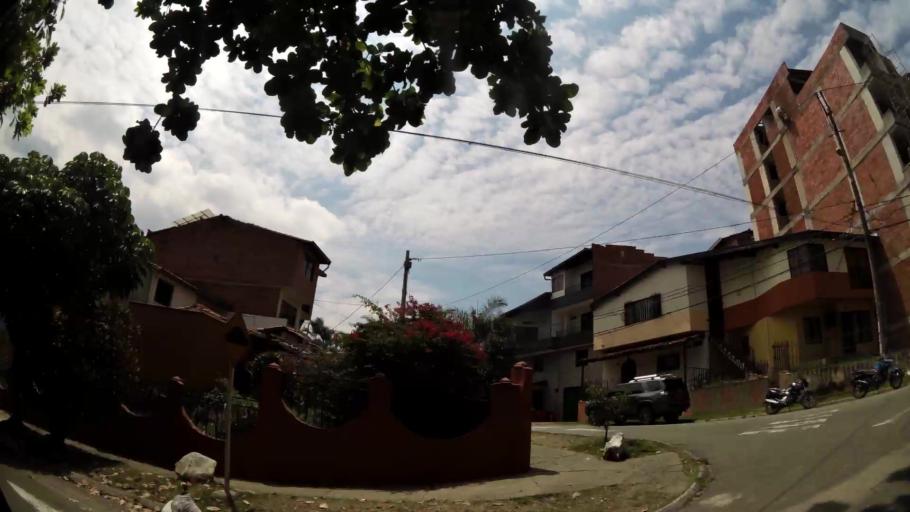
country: CO
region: Antioquia
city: Bello
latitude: 6.3169
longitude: -75.5657
